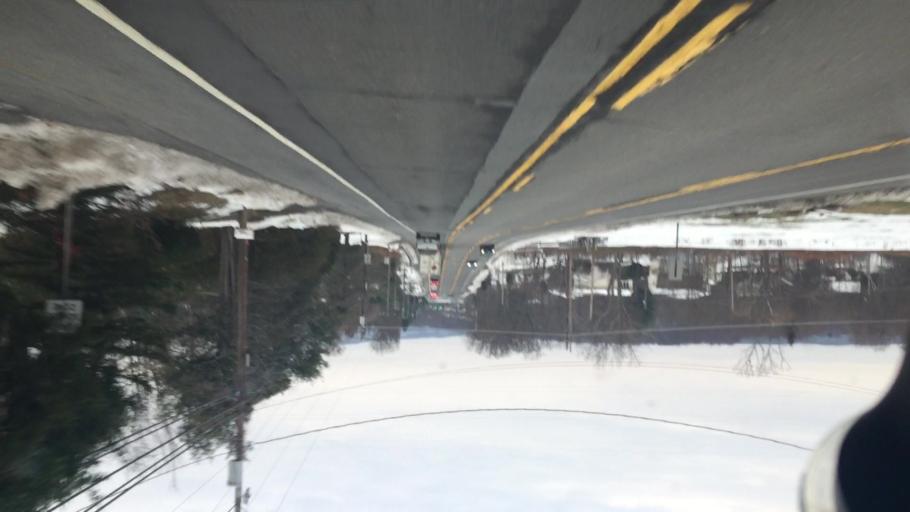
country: US
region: Pennsylvania
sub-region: Luzerne County
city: Mountain Top
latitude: 41.1399
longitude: -75.9015
